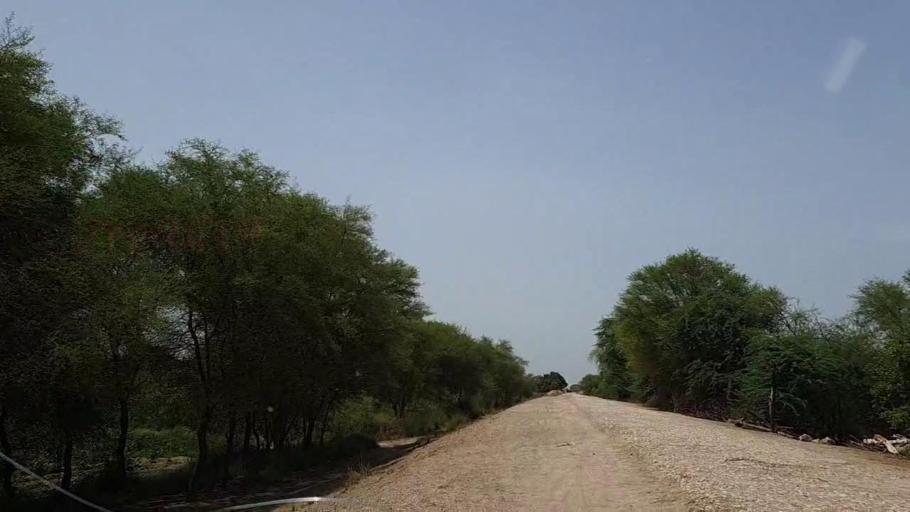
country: PK
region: Sindh
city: Tharu Shah
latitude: 27.0339
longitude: 68.1121
